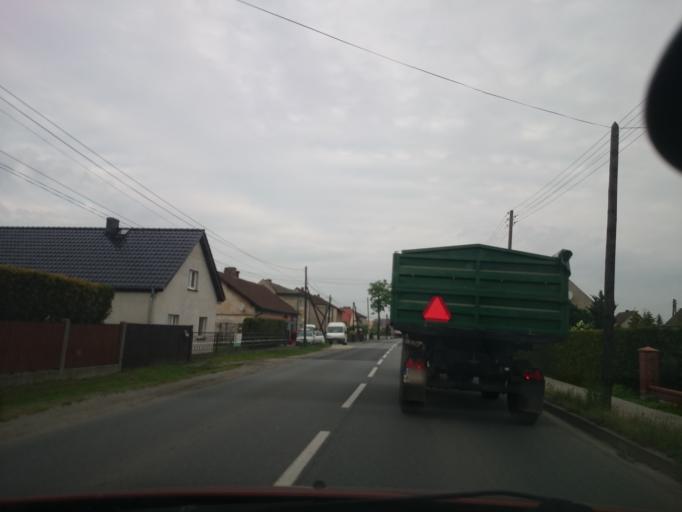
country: PL
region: Opole Voivodeship
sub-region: Powiat opolski
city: Dobrzen Wielki
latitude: 50.7553
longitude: 17.8495
